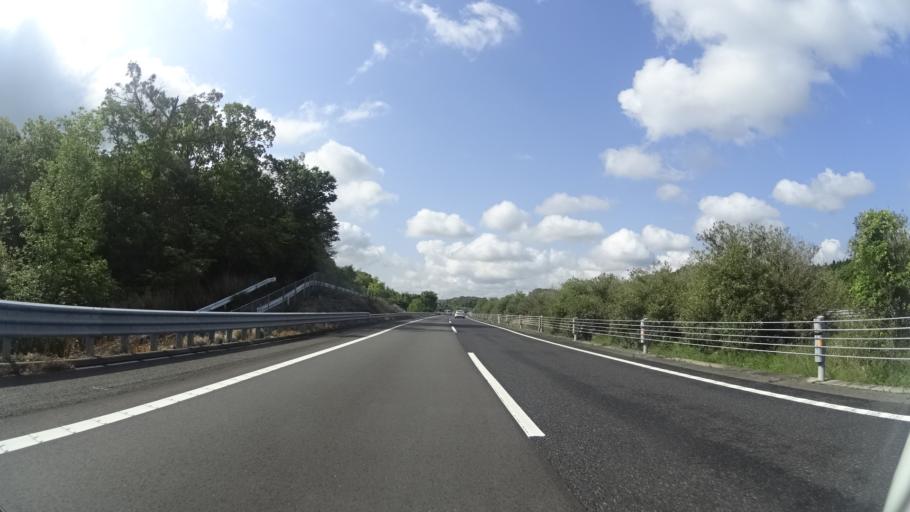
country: JP
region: Hyogo
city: Sumoto
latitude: 34.4536
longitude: 134.8780
